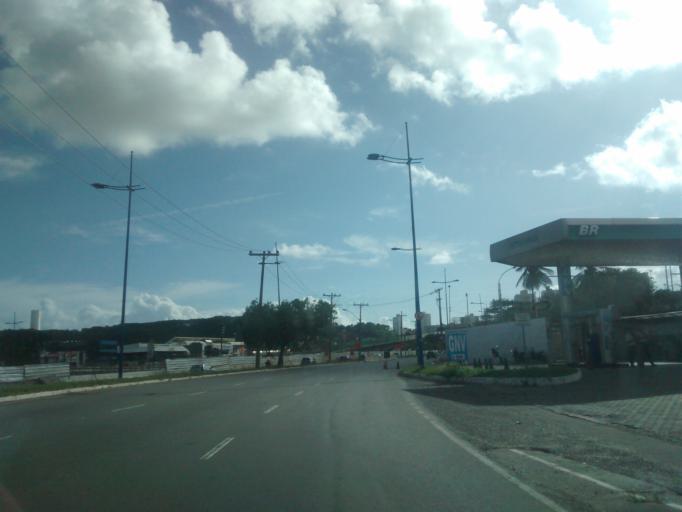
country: BR
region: Bahia
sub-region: Salvador
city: Salvador
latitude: -12.9793
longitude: -38.4657
